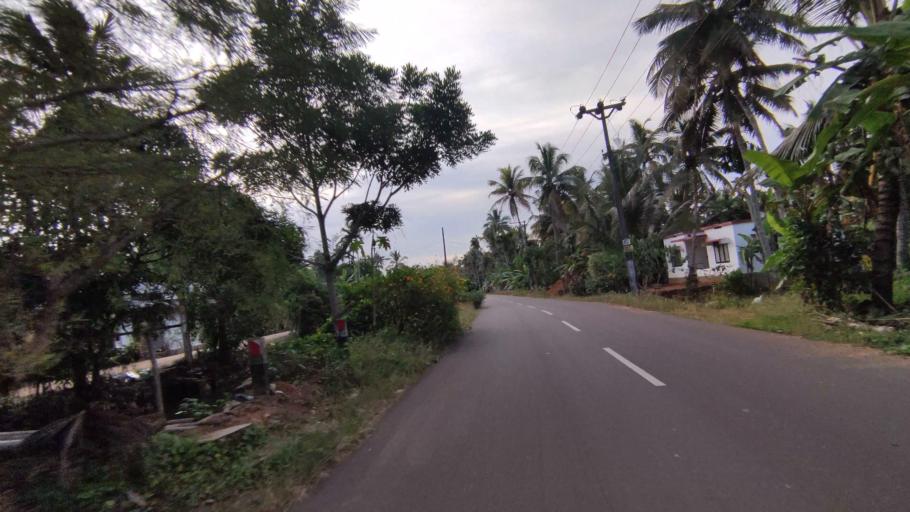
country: IN
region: Kerala
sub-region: Kottayam
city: Kottayam
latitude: 9.6441
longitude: 76.4833
